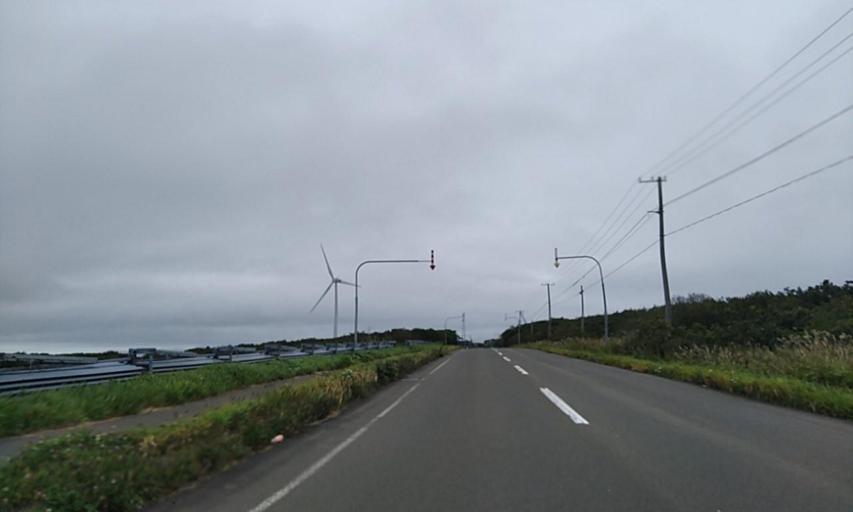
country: JP
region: Hokkaido
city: Nemuro
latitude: 43.3843
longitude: 145.6534
